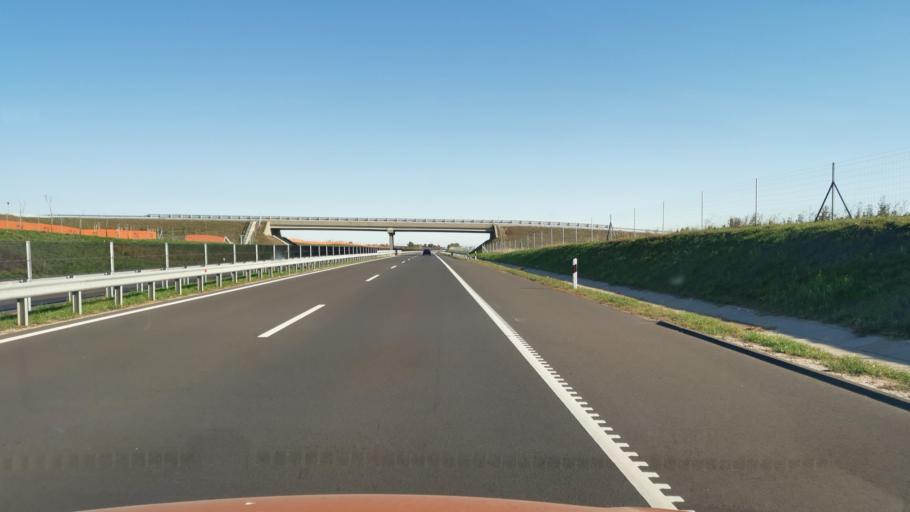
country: HU
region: Borsod-Abauj-Zemplen
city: Halmaj
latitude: 48.2772
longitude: 21.0059
